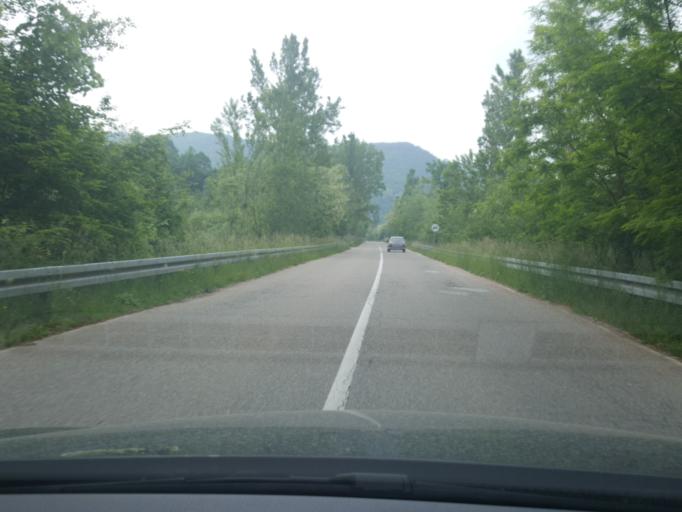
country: RS
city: Kamenica
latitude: 44.2185
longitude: 19.7163
